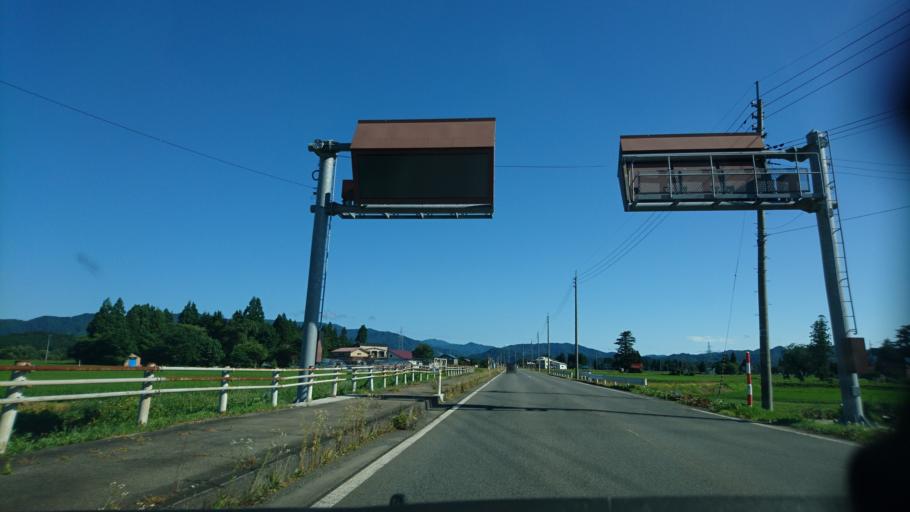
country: JP
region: Akita
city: Kakunodatemachi
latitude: 39.6228
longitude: 140.5718
